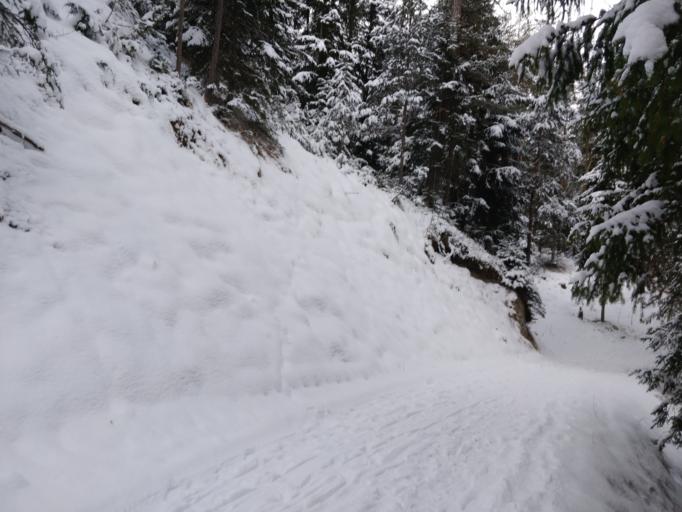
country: IT
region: Trentino-Alto Adige
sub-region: Bolzano
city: San Vigilio
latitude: 46.6954
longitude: 11.9290
